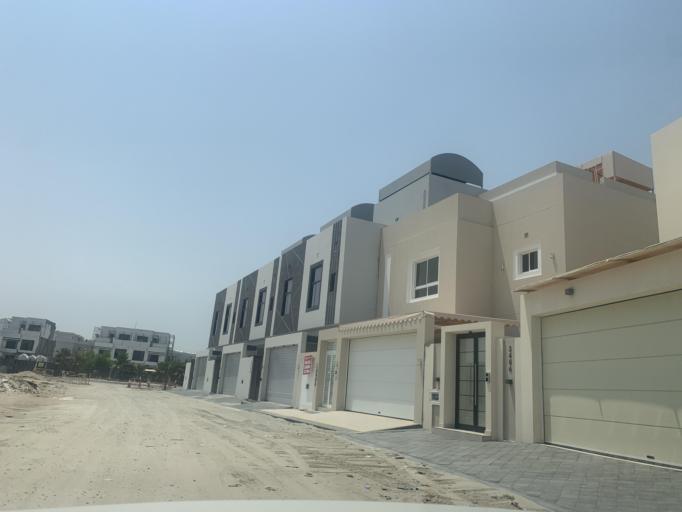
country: BH
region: Central Governorate
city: Madinat Hamad
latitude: 26.1459
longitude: 50.4655
